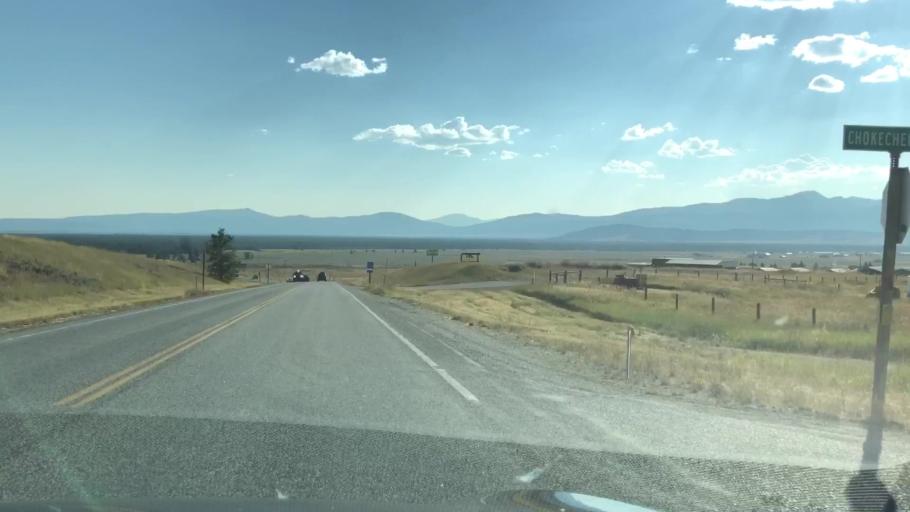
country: US
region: Montana
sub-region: Gallatin County
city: West Yellowstone
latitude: 44.7915
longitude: -111.1099
